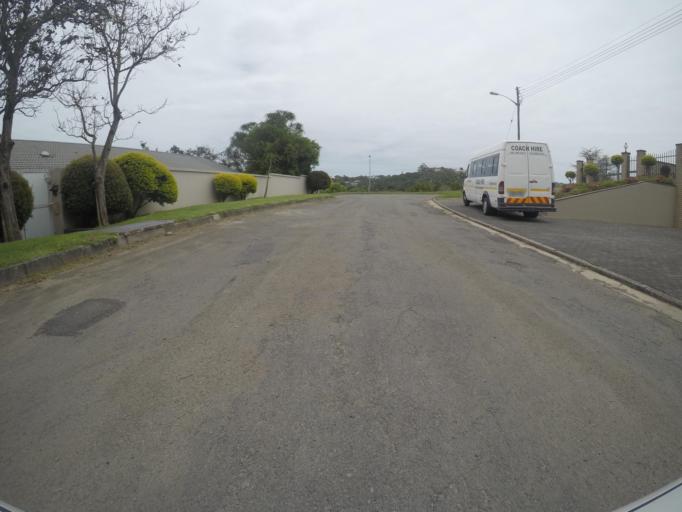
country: ZA
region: Eastern Cape
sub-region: Buffalo City Metropolitan Municipality
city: East London
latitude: -32.9739
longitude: 27.9334
